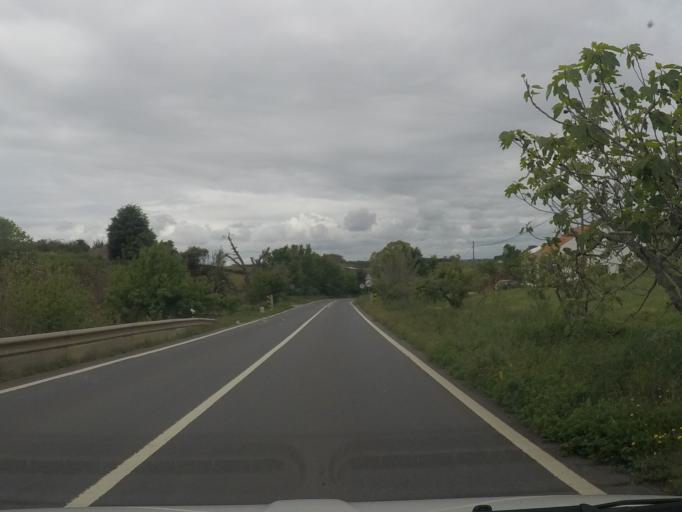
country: PT
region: Setubal
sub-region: Santiago do Cacem
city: Cercal
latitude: 37.8154
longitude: -8.6835
